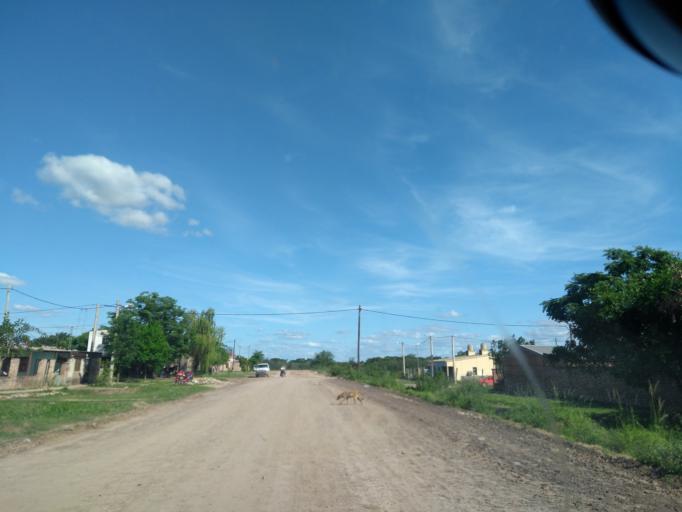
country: AR
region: Chaco
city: Resistencia
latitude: -27.4523
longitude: -58.9623
